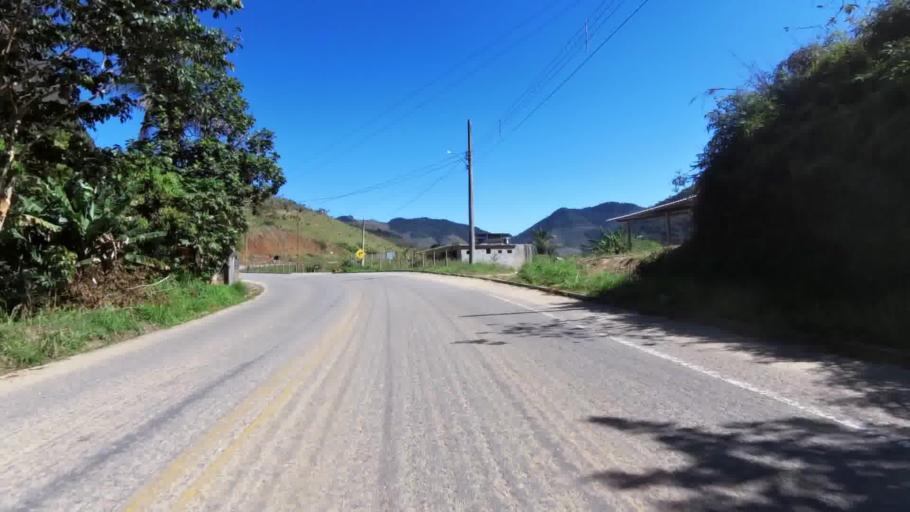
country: BR
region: Espirito Santo
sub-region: Vargem Alta
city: Vargem Alta
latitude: -20.7160
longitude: -40.9093
